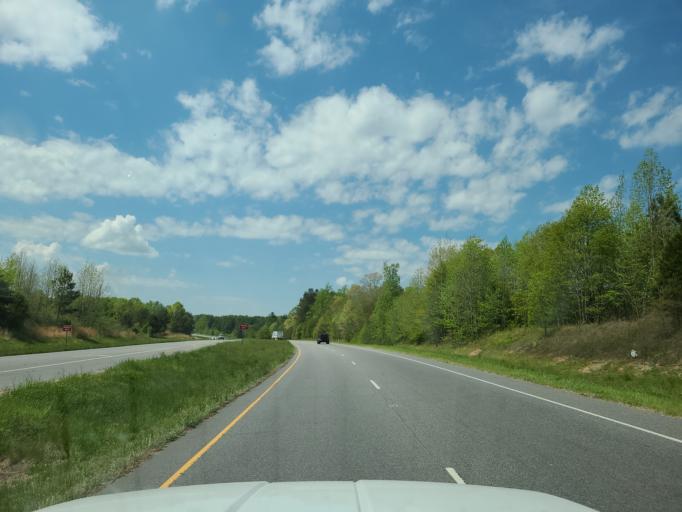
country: US
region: North Carolina
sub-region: Lincoln County
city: Lincolnton
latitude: 35.4267
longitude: -81.3080
